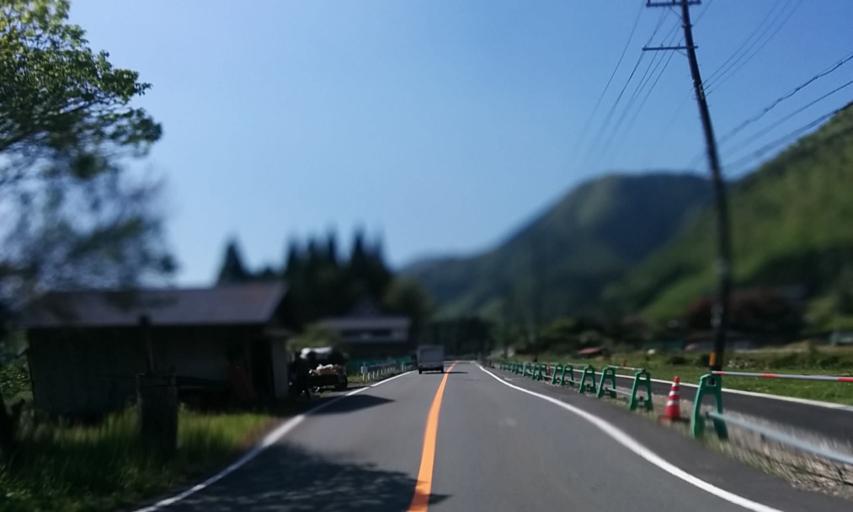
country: JP
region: Kyoto
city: Maizuru
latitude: 35.2756
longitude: 135.5447
